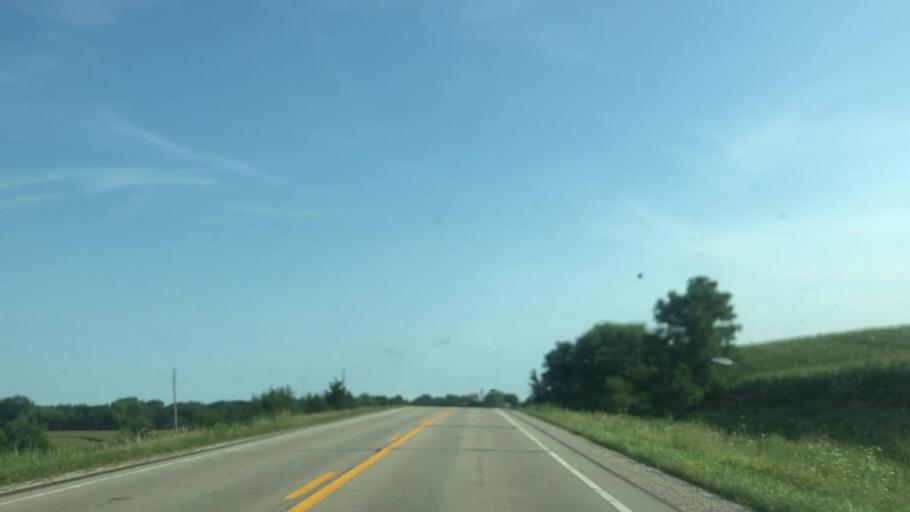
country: US
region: Iowa
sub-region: Marshall County
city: Marshalltown
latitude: 42.0356
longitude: -93.0000
